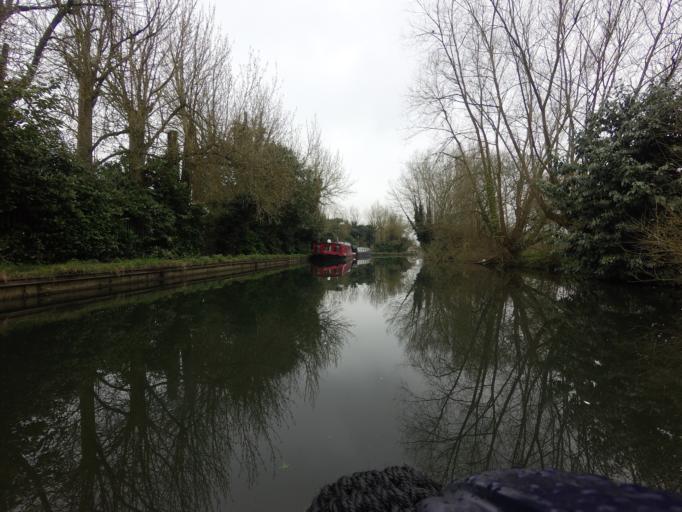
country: GB
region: England
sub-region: Hertfordshire
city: Kings Langley
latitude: 51.7181
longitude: -0.4464
